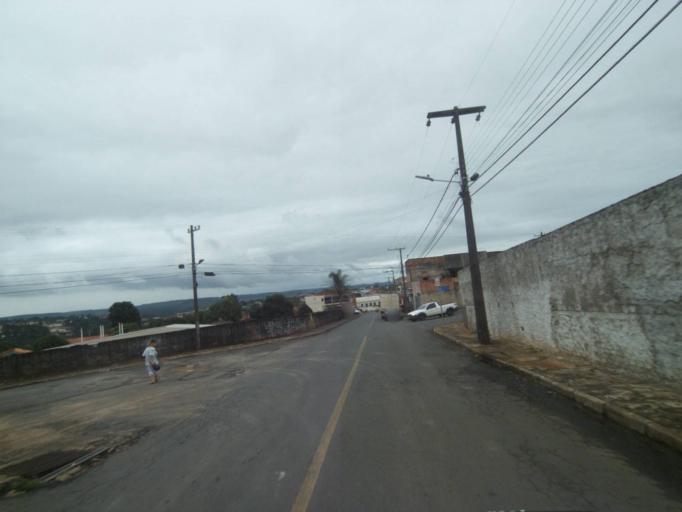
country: BR
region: Parana
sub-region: Telemaco Borba
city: Telemaco Borba
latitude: -24.3275
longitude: -50.6428
